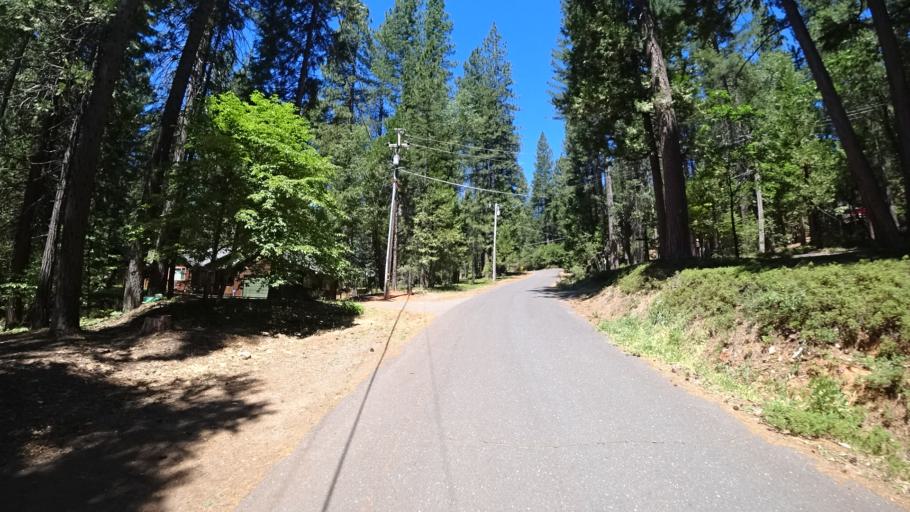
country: US
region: California
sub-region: Calaveras County
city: Arnold
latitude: 38.2359
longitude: -120.3352
